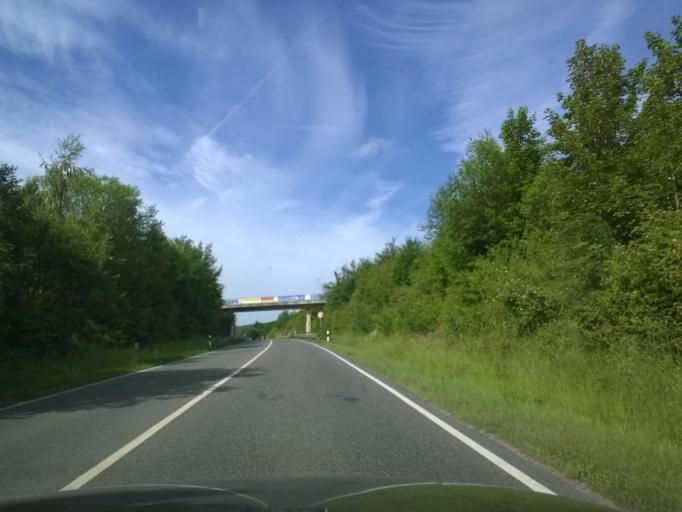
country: DE
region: Lower Saxony
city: Diekholzen
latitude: 52.1180
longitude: 9.9410
